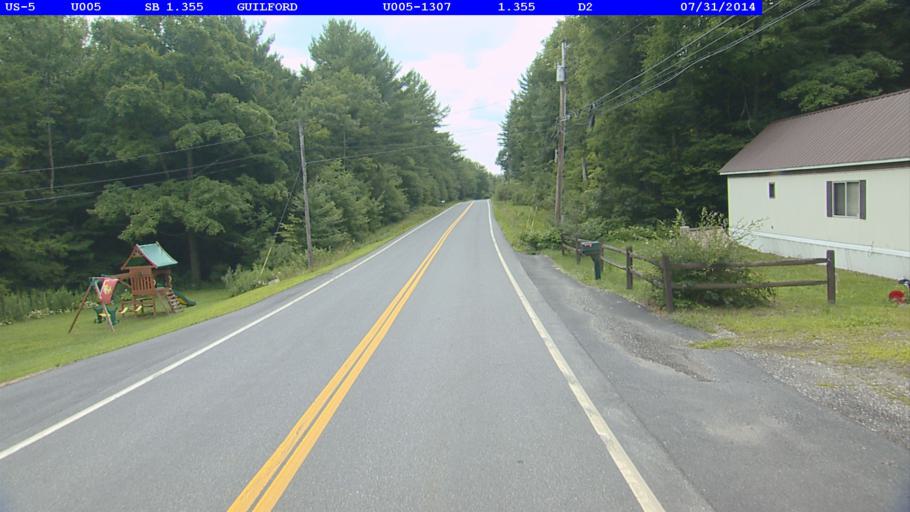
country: US
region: Massachusetts
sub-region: Franklin County
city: Bernardston
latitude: 42.7491
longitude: -72.5695
